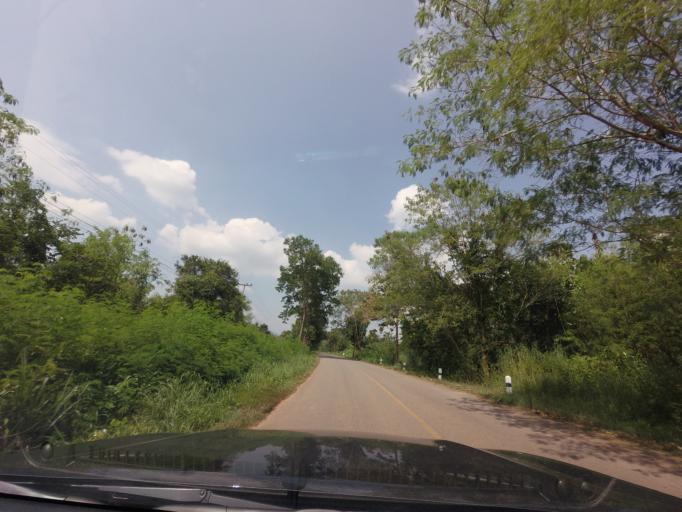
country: TH
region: Uttaradit
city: Fak Tha
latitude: 17.8979
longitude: 100.9784
